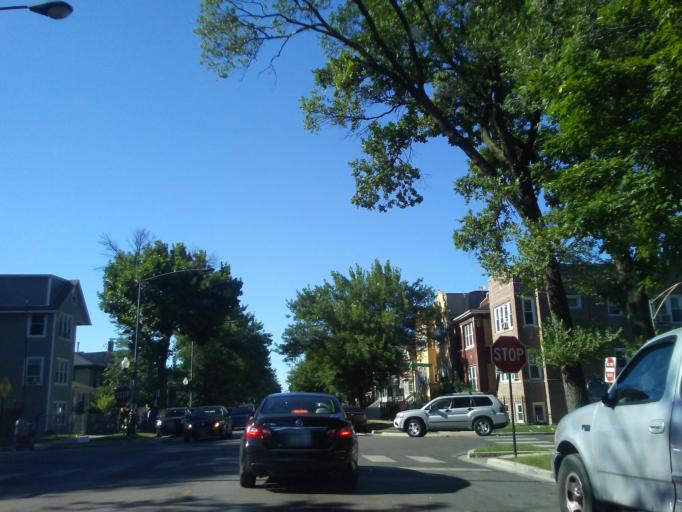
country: US
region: Illinois
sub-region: Cook County
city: Oak Park
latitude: 41.9186
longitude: -87.7364
